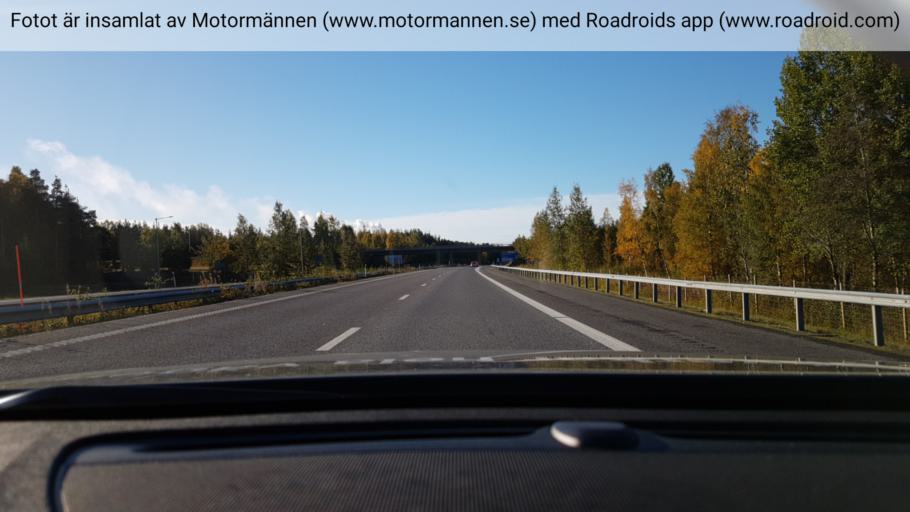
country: SE
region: Norrbotten
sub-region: Pitea Kommun
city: Pitea
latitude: 65.3346
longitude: 21.4412
